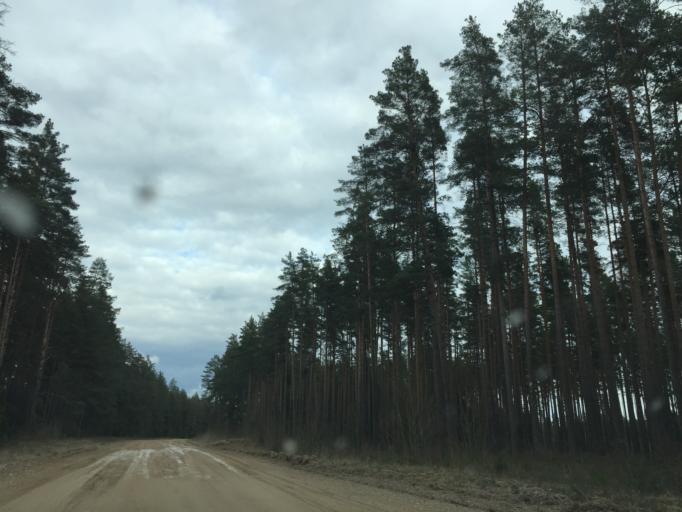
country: LV
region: Lielvarde
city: Lielvarde
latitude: 56.5385
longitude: 24.8303
